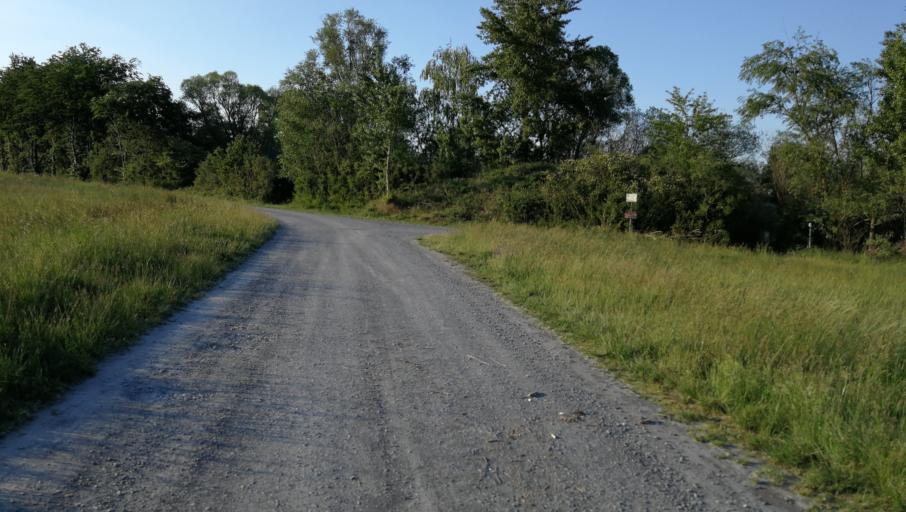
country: DE
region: Baden-Wuerttemberg
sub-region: Karlsruhe Region
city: Altlussheim
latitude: 49.3159
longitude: 8.4885
